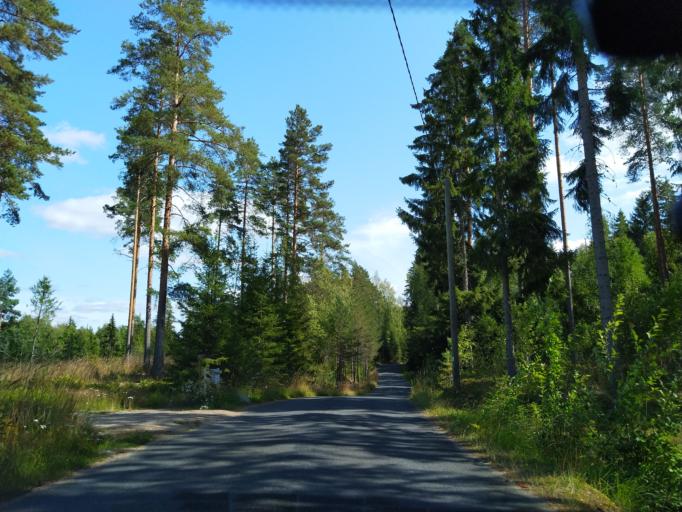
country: FI
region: Uusimaa
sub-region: Helsinki
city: Karkkila
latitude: 60.7203
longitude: 24.1785
